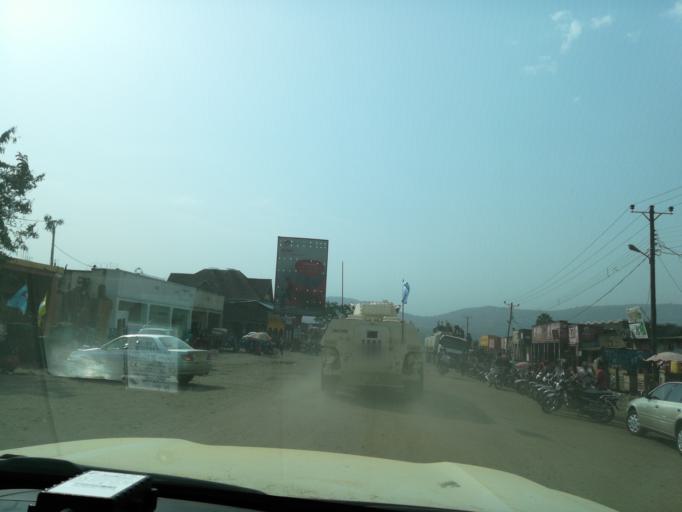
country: UG
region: Western Region
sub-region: Kasese District
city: Kilembe
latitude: 0.0421
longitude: 29.7145
